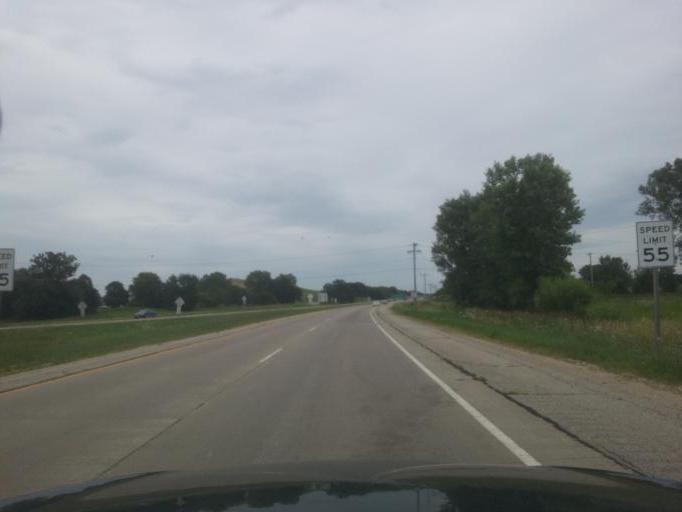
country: US
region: Wisconsin
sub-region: Dane County
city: McFarland
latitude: 43.0452
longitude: -89.2677
